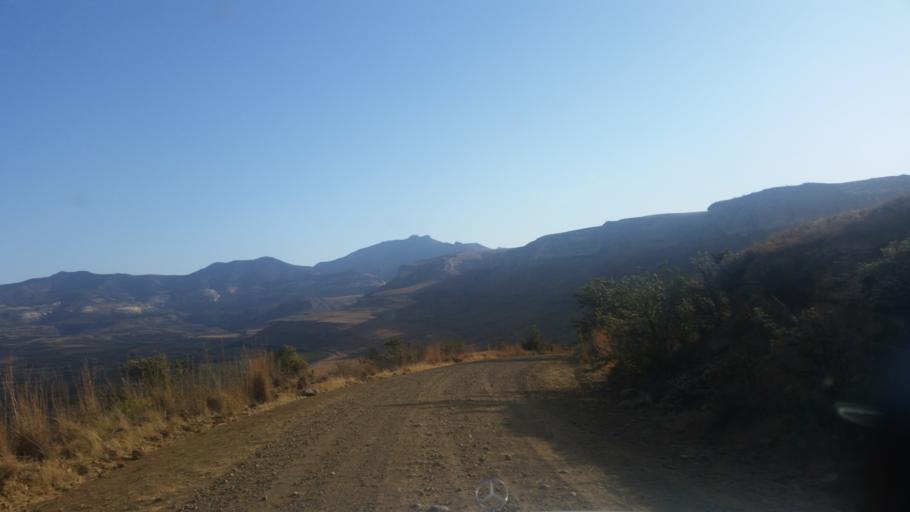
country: ZA
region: Orange Free State
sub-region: Thabo Mofutsanyana District Municipality
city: Phuthaditjhaba
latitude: -28.4916
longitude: 28.6956
